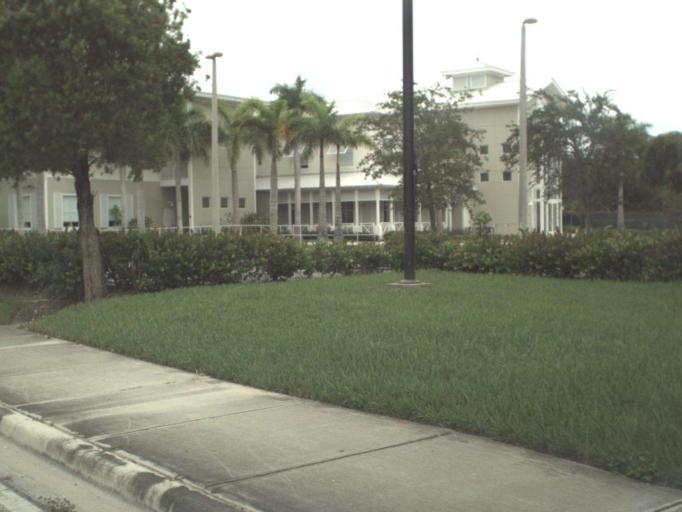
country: US
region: Florida
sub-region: Miami-Dade County
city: North Miami Beach
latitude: 25.9210
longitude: -80.1551
